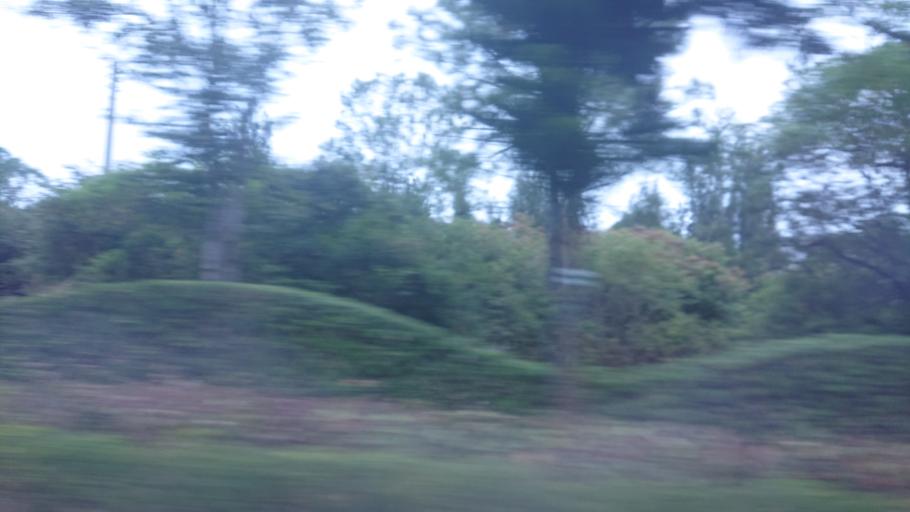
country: TW
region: Fukien
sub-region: Kinmen
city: Jincheng
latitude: 24.4129
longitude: 118.2888
